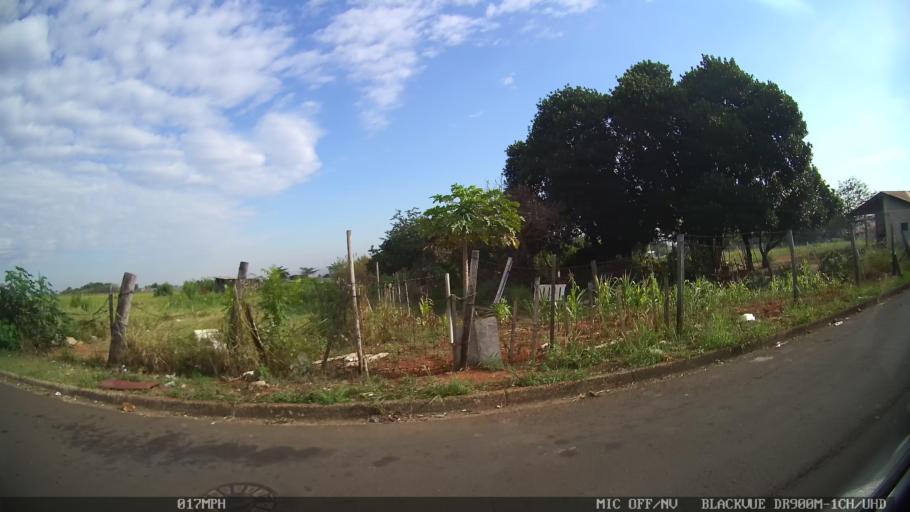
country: BR
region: Sao Paulo
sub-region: Americana
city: Americana
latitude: -22.7192
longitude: -47.3687
